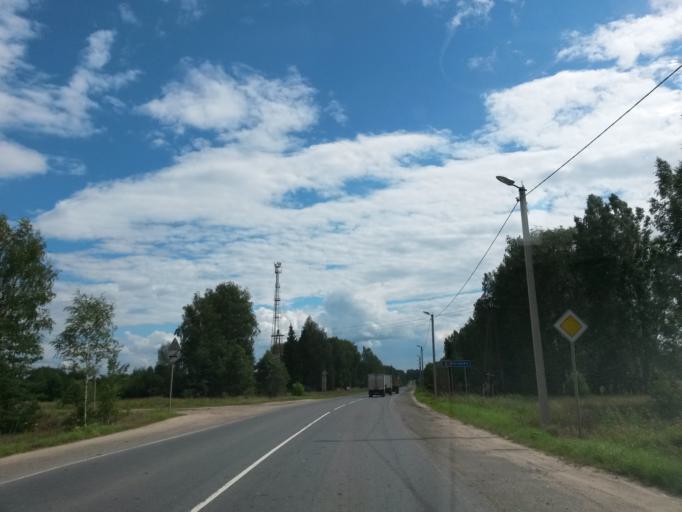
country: RU
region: Ivanovo
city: Novo-Talitsy
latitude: 57.0628
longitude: 40.7158
